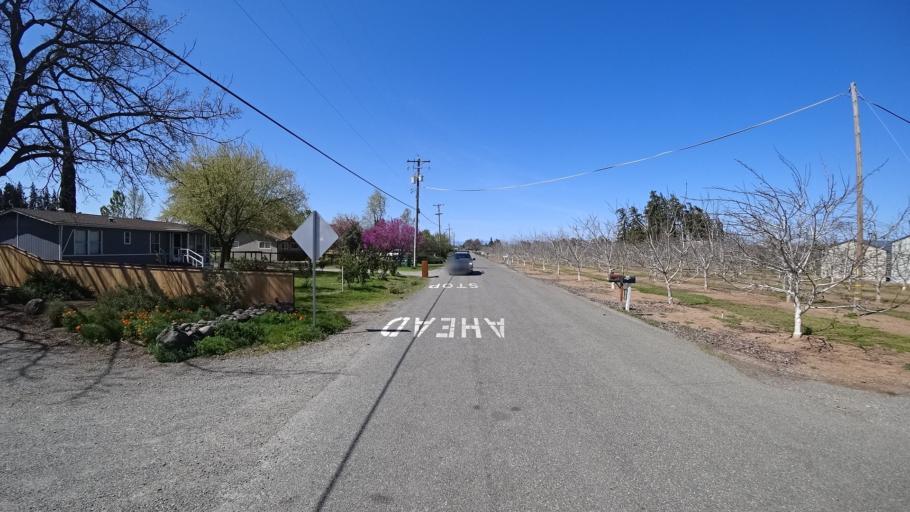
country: US
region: California
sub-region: Glenn County
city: Hamilton City
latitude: 39.7969
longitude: -122.0686
